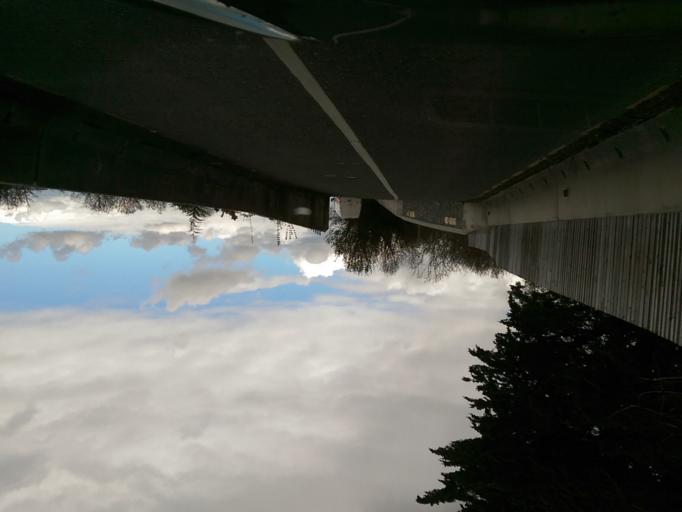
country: IE
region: Leinster
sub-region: An Mhi
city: Dunboyne
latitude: 53.3895
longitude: -6.4493
